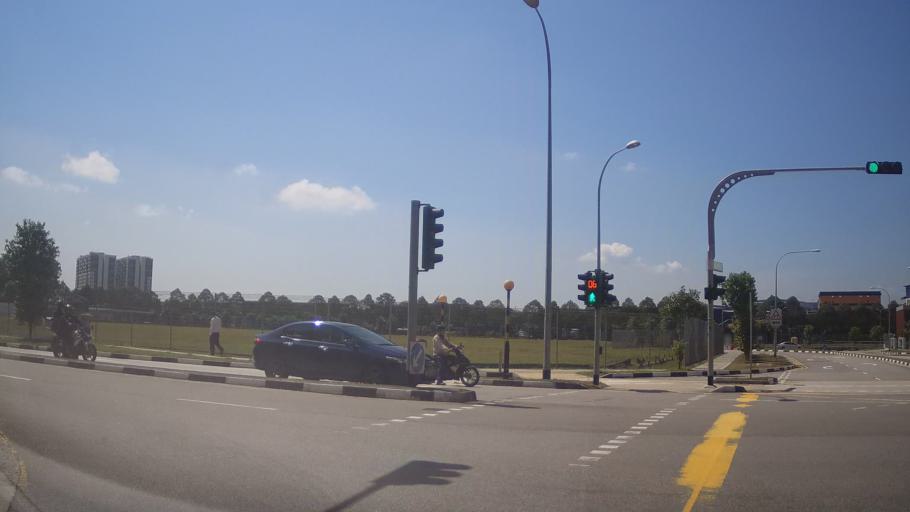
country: SG
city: Singapore
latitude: 1.3266
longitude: 103.7228
